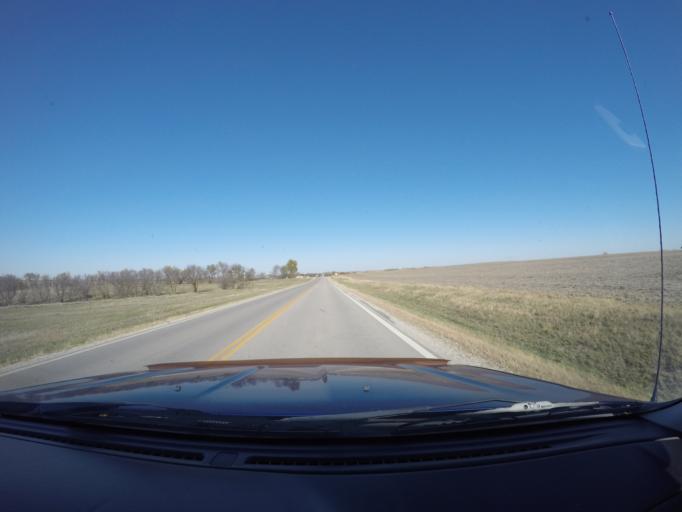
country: US
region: Kansas
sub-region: Marshall County
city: Marysville
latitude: 39.8509
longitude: -96.4170
